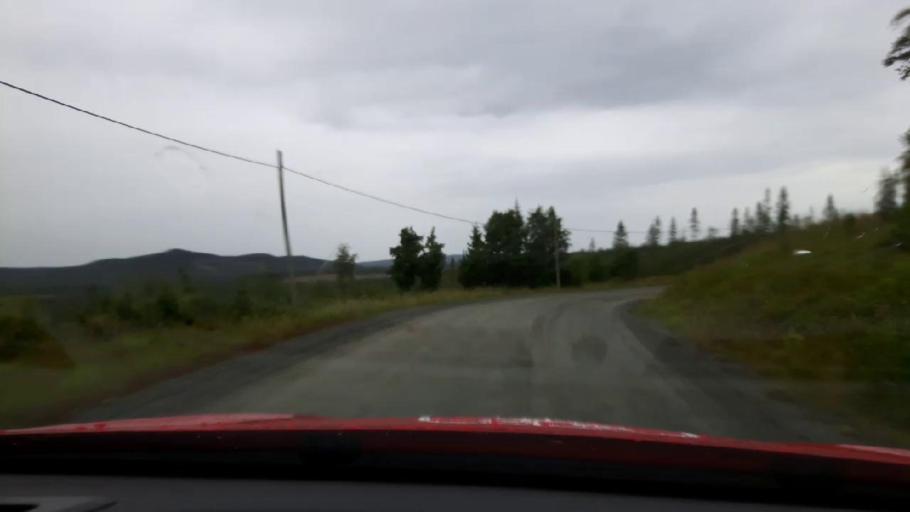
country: SE
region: Jaemtland
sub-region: Are Kommun
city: Are
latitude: 63.4192
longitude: 12.8245
